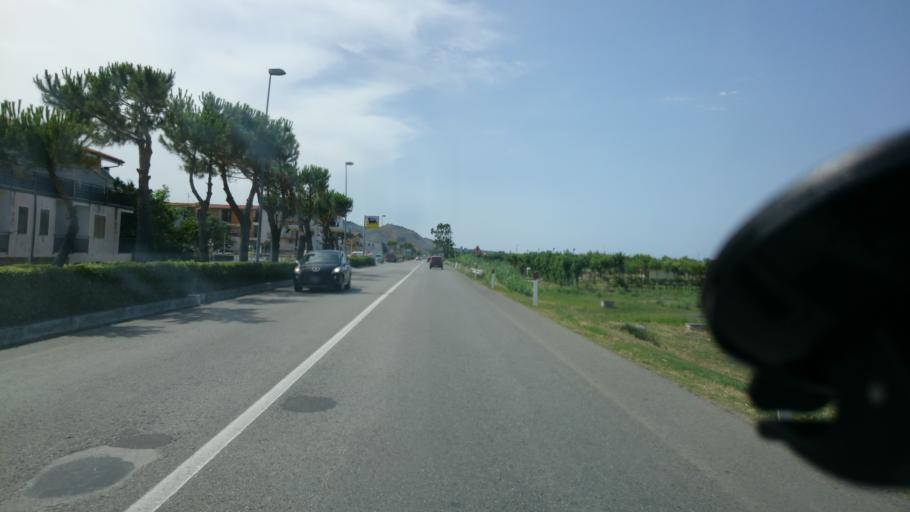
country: IT
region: Calabria
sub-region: Provincia di Cosenza
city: Marcellina
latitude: 39.7491
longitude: 15.8061
